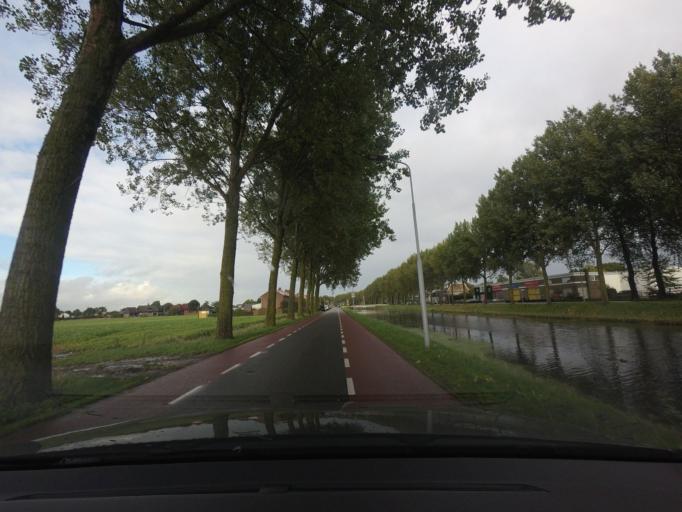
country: NL
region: South Holland
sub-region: Gemeente Lisse
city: Lisse
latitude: 52.2332
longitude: 4.5871
